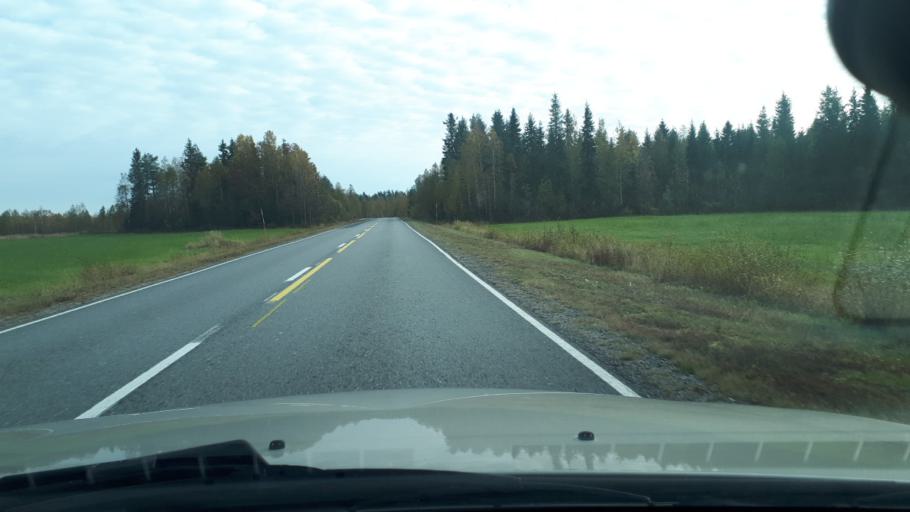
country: FI
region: Lapland
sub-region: Rovaniemi
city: Ranua
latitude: 65.9610
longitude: 26.0564
